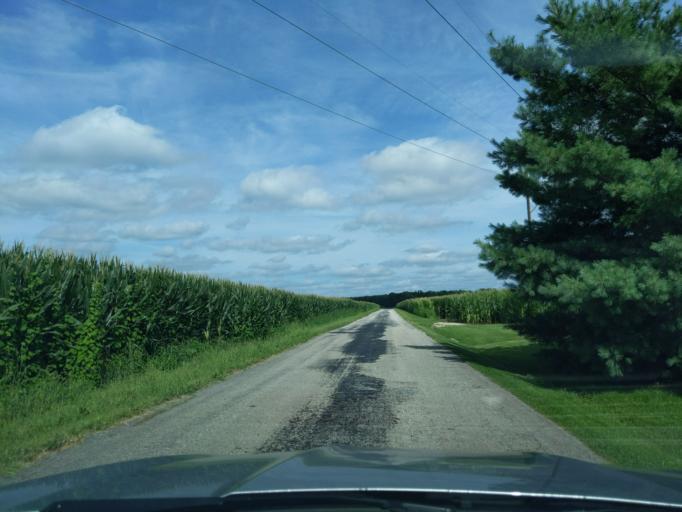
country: US
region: Indiana
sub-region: Ripley County
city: Osgood
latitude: 39.2354
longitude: -85.3698
